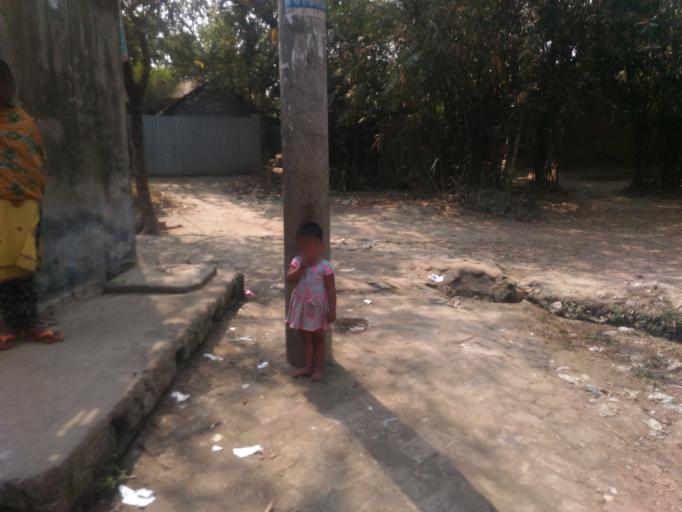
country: BD
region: Dhaka
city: Tungi
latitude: 24.0109
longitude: 90.3799
